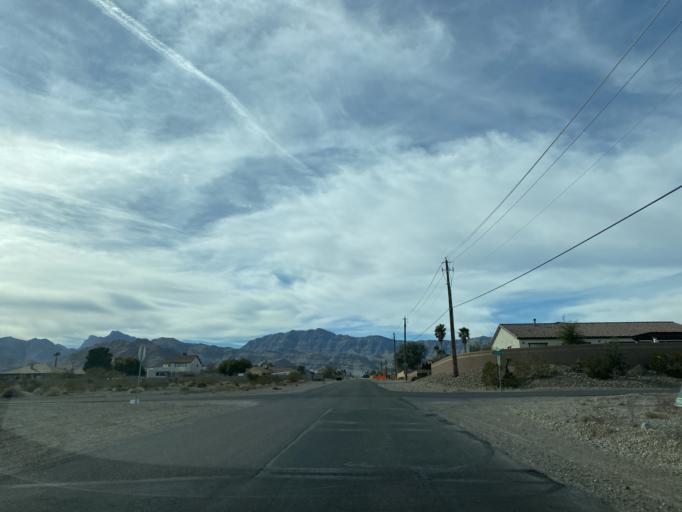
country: US
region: Nevada
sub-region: Clark County
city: Summerlin South
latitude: 36.2700
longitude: -115.3147
